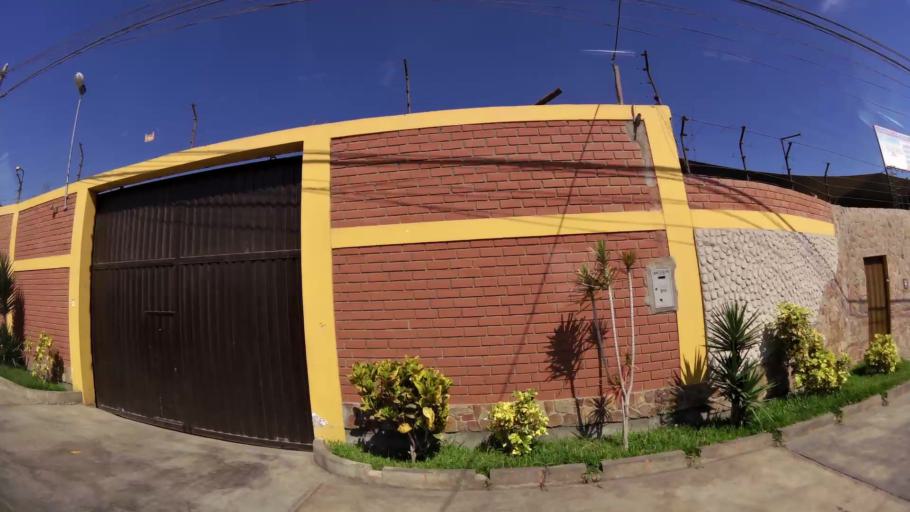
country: PE
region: Ica
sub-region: Provincia de Chincha
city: Sunampe
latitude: -13.4178
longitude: -76.1586
